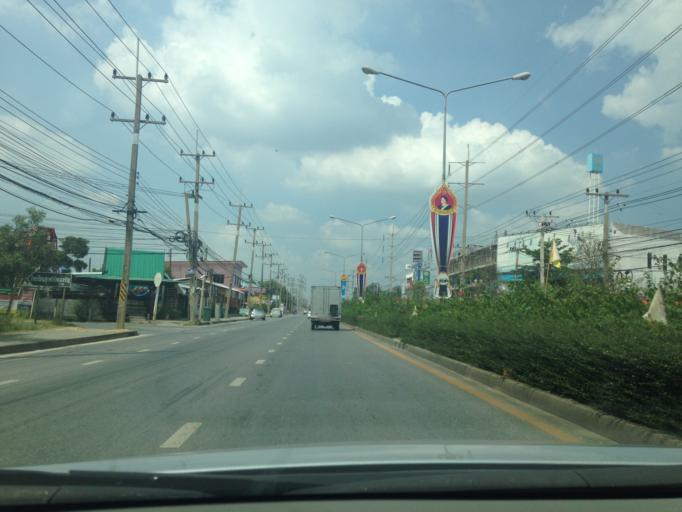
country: TH
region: Pathum Thani
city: Sam Khok
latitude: 14.0604
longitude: 100.5238
